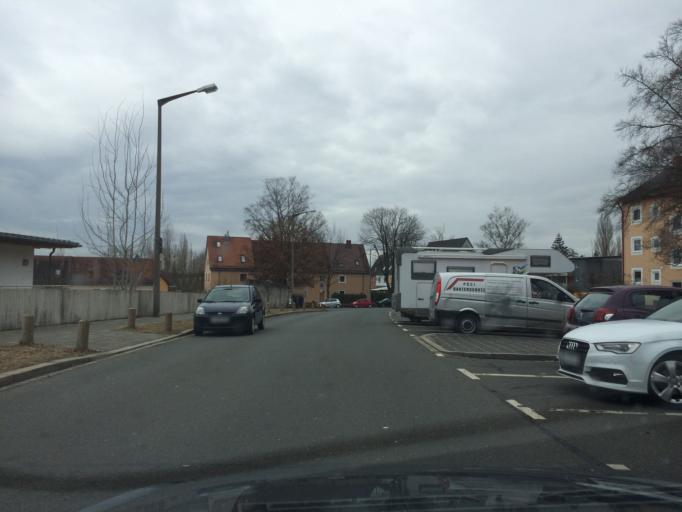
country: DE
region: Bavaria
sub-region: Regierungsbezirk Mittelfranken
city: Nuernberg
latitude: 49.4284
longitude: 11.0944
